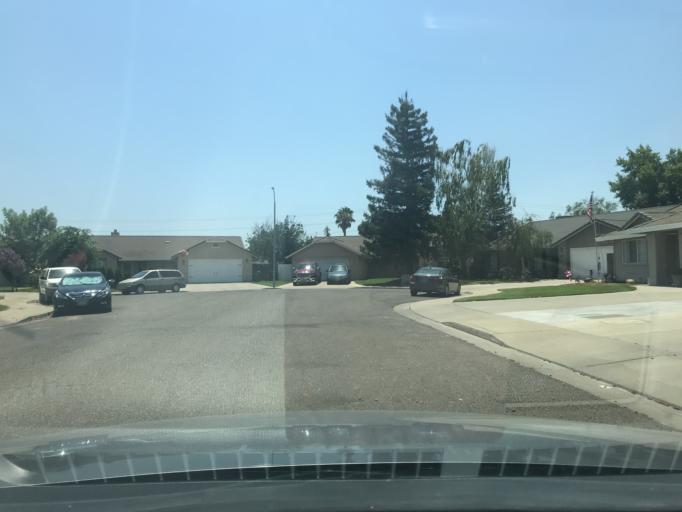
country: US
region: California
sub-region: Merced County
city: Atwater
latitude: 37.3692
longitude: -120.5922
